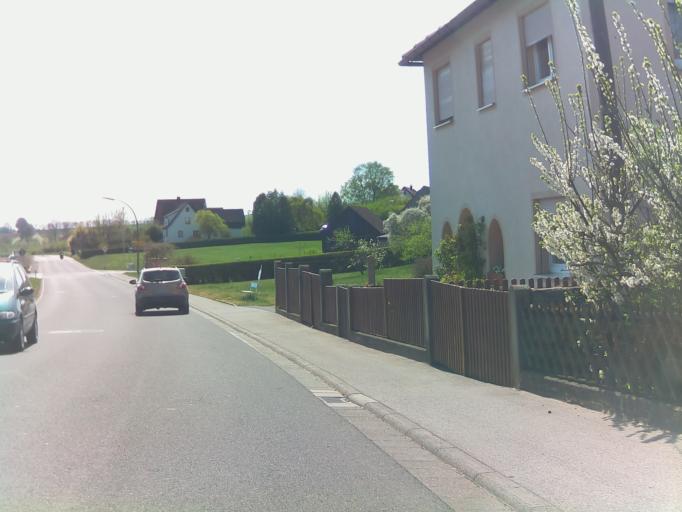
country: DE
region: Bavaria
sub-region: Regierungsbezirk Unterfranken
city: Ermershausen
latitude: 50.2089
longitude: 10.6222
